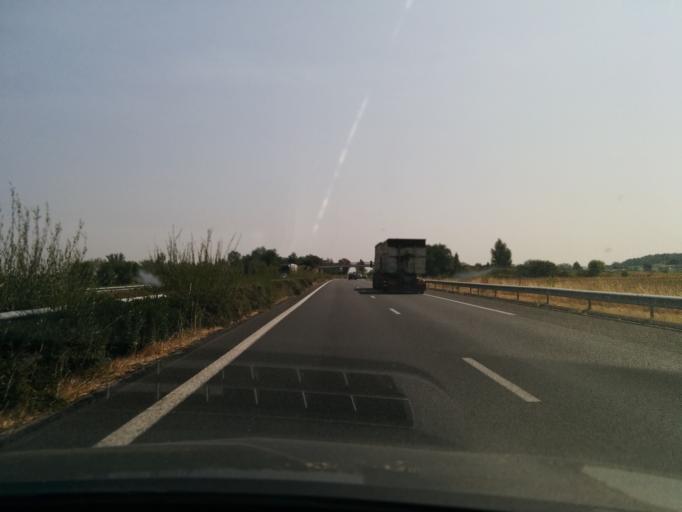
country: FR
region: Midi-Pyrenees
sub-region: Departement du Tarn
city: Brens
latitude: 43.8877
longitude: 1.9501
